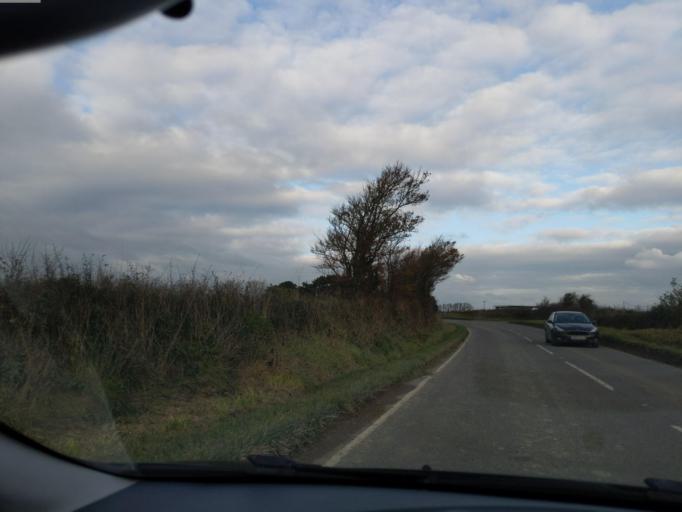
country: GB
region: England
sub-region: Cornwall
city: Padstow
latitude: 50.5291
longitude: -4.9529
